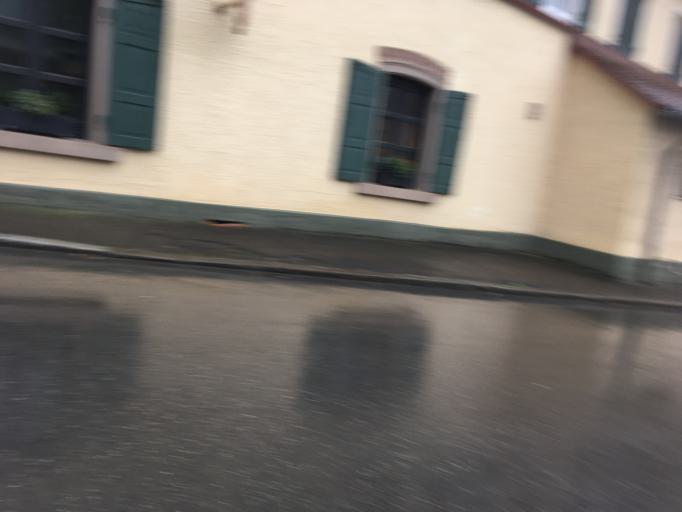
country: DE
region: Baden-Wuerttemberg
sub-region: Tuebingen Region
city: Mossingen
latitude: 48.4089
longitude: 9.0628
